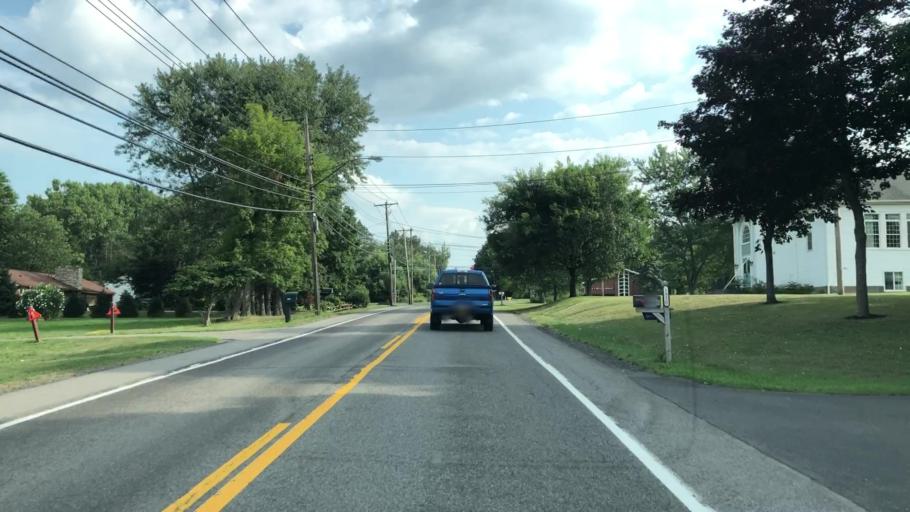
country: US
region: New York
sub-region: Erie County
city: Elma Center
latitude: 42.8239
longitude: -78.6367
